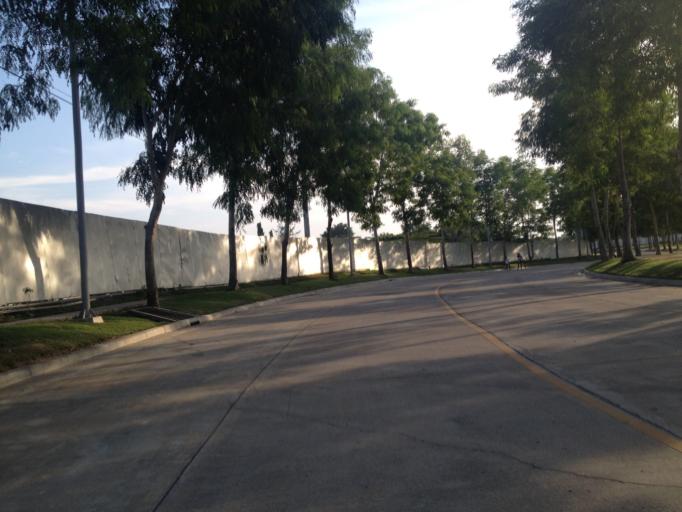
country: TH
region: Chiang Mai
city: Chiang Mai
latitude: 18.7553
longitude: 98.9554
